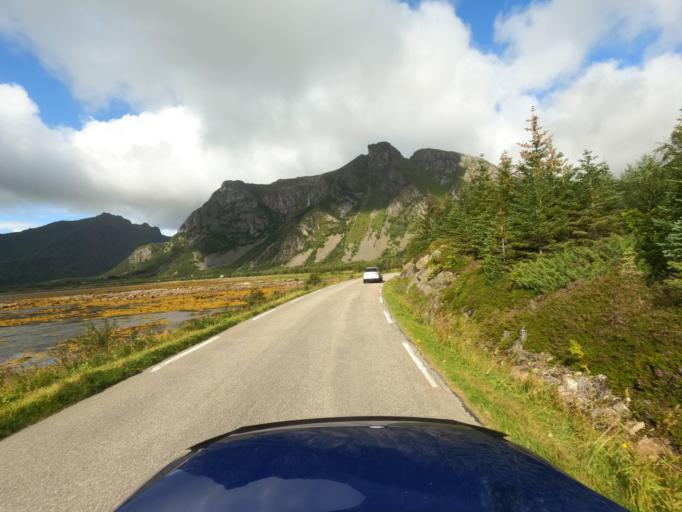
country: NO
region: Nordland
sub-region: Vestvagoy
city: Evjen
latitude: 68.1974
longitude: 13.9962
